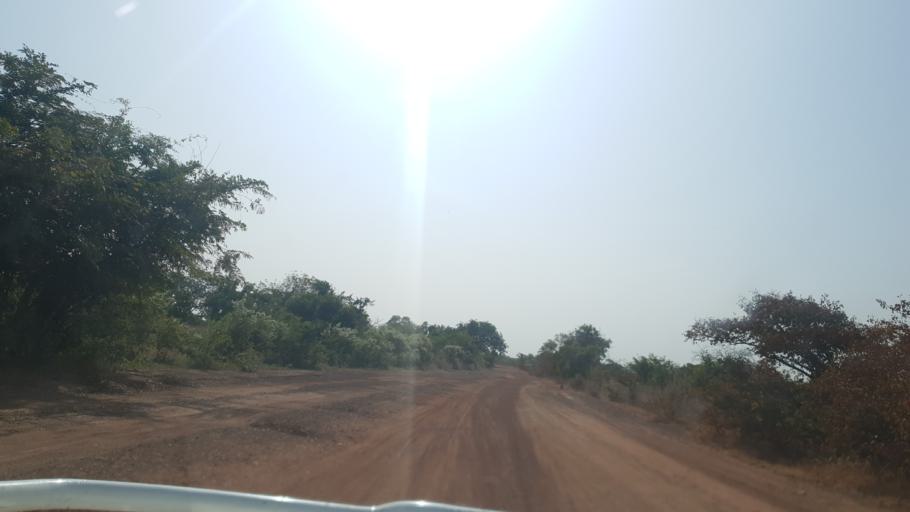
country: ML
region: Koulikoro
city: Dioila
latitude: 12.6701
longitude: -6.7027
